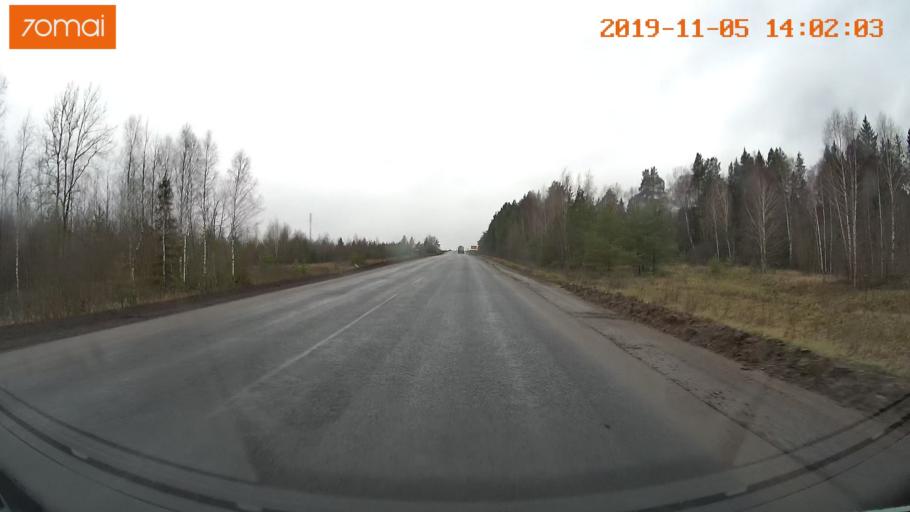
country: RU
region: Ivanovo
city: Kokhma
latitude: 57.0048
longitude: 41.2204
